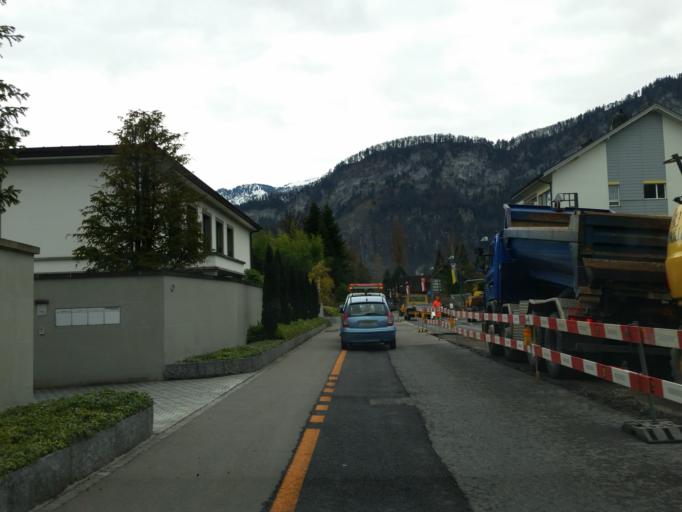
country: CH
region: Nidwalden
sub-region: Nidwalden
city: Hergiswil
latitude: 46.9925
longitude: 8.3144
